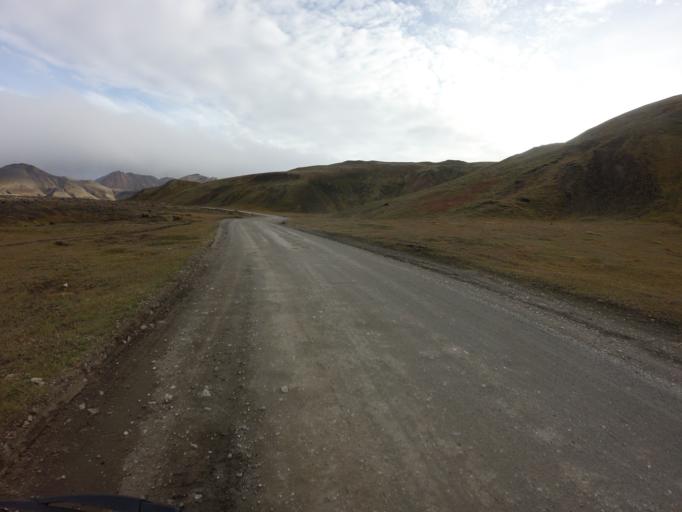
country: IS
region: South
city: Vestmannaeyjar
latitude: 64.0085
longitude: -19.0420
